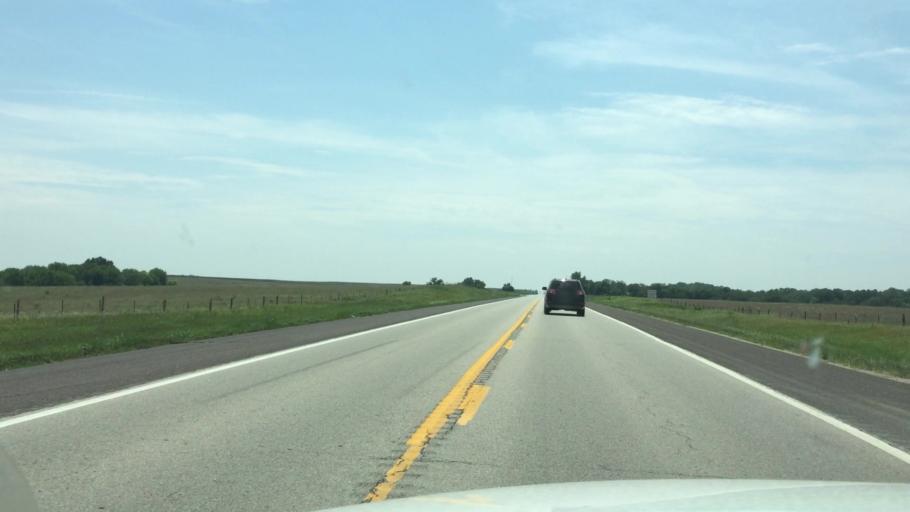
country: US
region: Kansas
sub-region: Jackson County
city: Holton
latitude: 39.5212
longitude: -95.7482
